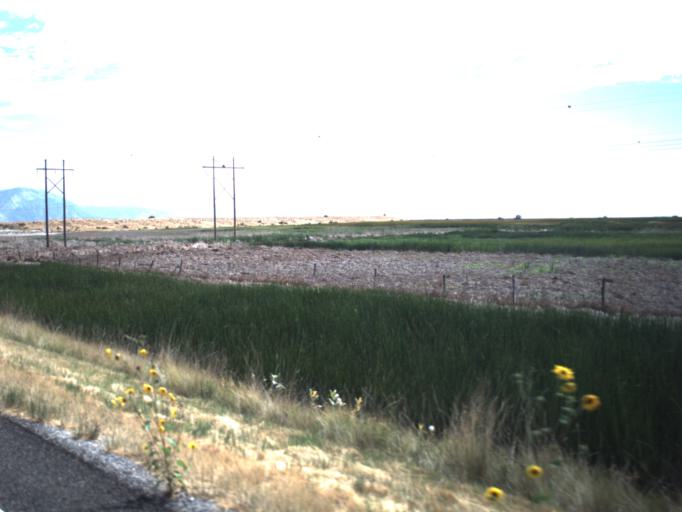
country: US
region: Utah
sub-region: Box Elder County
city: Tremonton
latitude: 41.6063
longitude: -112.3220
